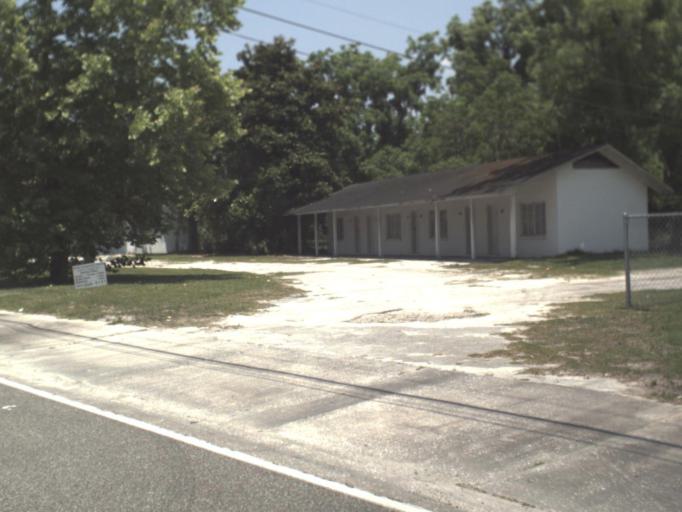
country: US
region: Florida
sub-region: Bradford County
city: Starke
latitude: 29.9647
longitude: -82.1040
